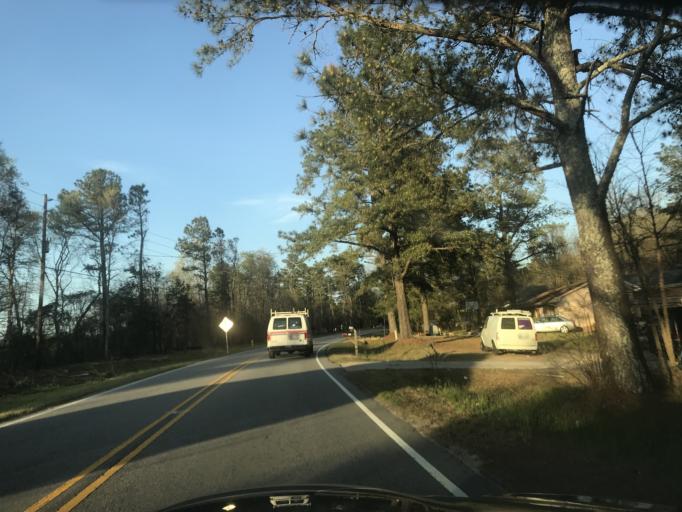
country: US
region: North Carolina
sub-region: Wake County
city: Garner
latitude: 35.7389
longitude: -78.5487
